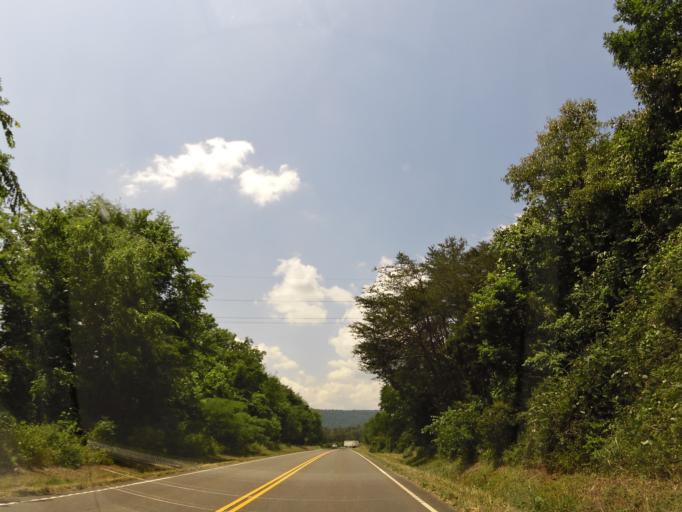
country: US
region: Tennessee
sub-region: Rhea County
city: Spring City
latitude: 35.6498
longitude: -84.8674
